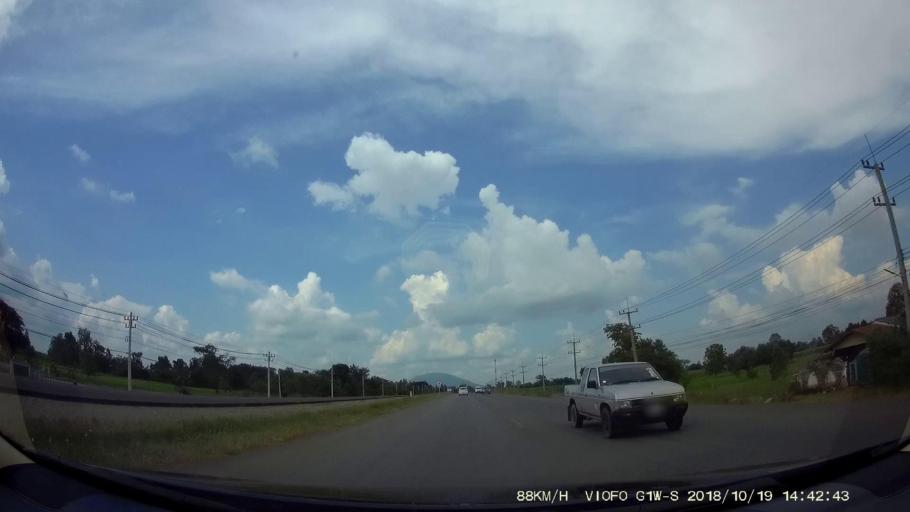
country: TH
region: Chaiyaphum
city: Phu Khiao
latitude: 16.2716
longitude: 102.2039
